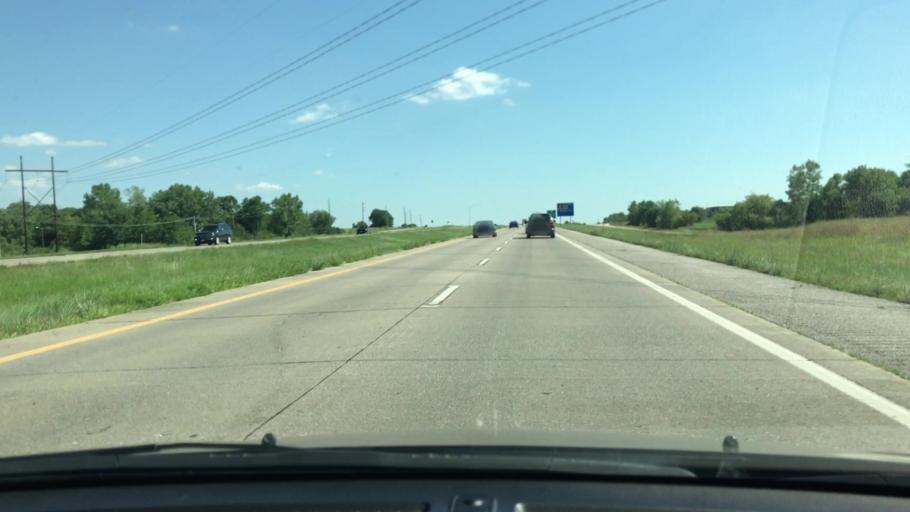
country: US
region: Missouri
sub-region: Jackson County
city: Greenwood
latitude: 38.8622
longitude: -94.3754
